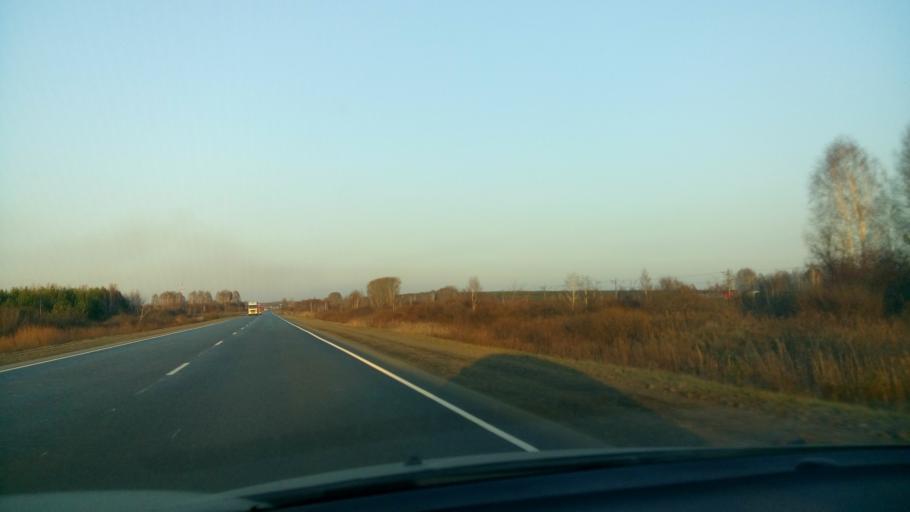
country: RU
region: Sverdlovsk
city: Obukhovskoye
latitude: 56.8292
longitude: 62.5627
